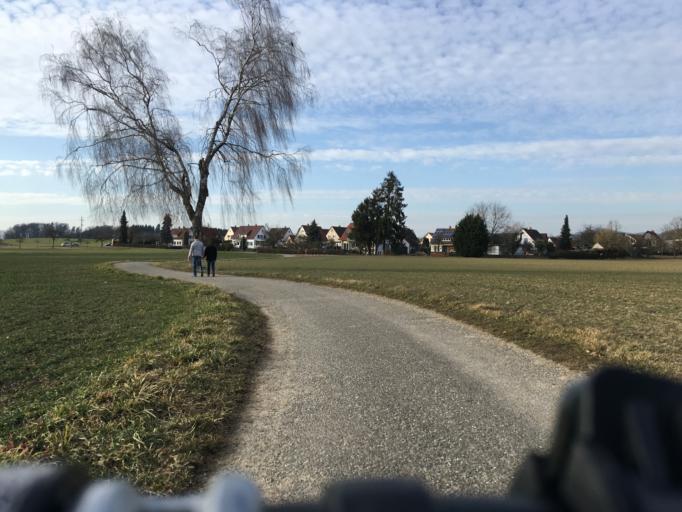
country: DE
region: Baden-Wuerttemberg
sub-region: Freiburg Region
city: Gottmadingen
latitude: 47.7265
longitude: 8.7590
